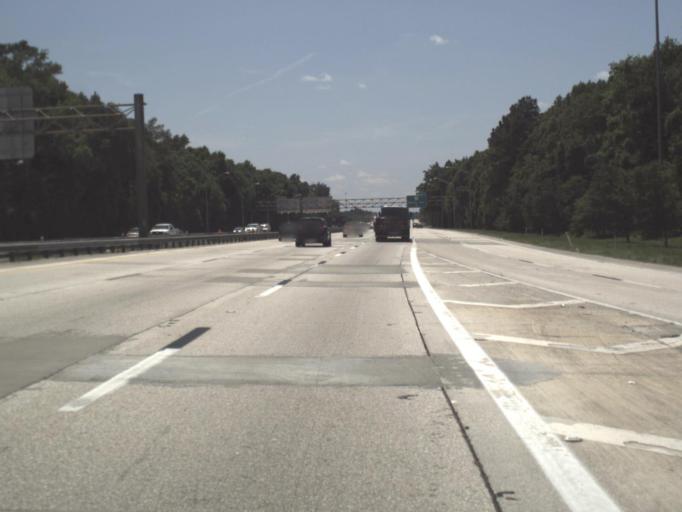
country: US
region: Florida
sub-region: Saint Johns County
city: Fruit Cove
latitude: 30.1951
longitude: -81.5565
